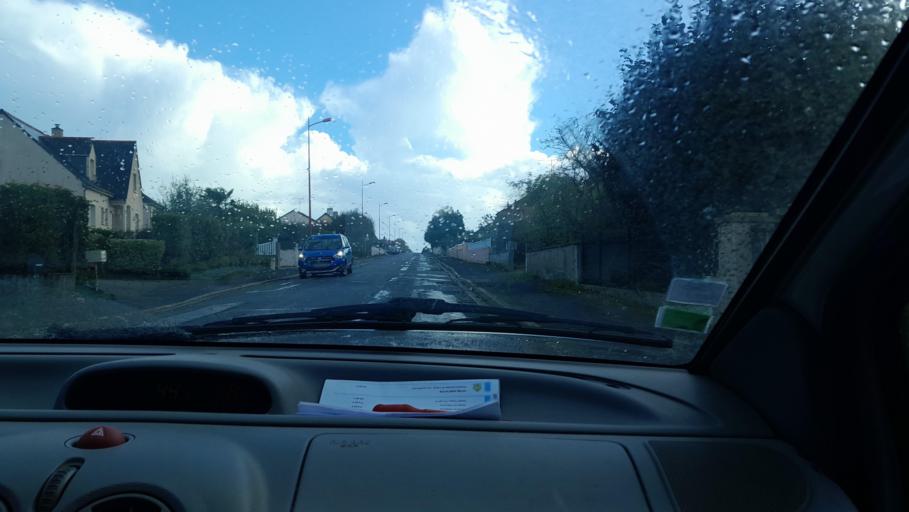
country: FR
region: Pays de la Loire
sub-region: Departement de la Mayenne
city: Cosse-le-Vivien
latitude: 47.9430
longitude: -0.9073
